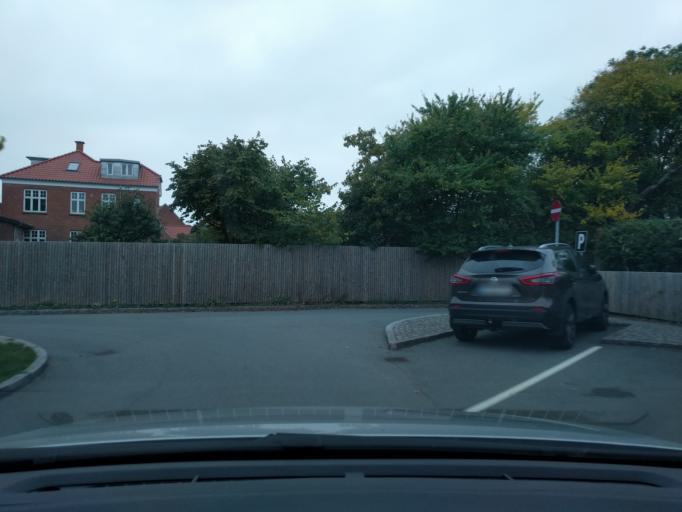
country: DK
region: South Denmark
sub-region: Svendborg Kommune
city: Svendborg
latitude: 55.0590
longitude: 10.6029
